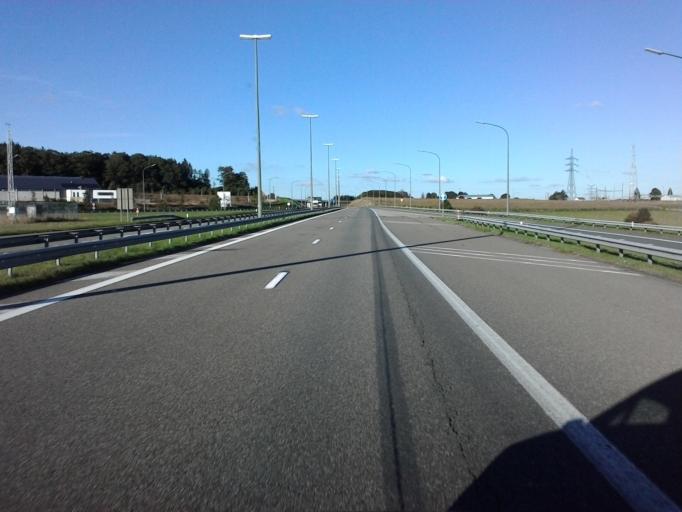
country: BE
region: Wallonia
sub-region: Province du Luxembourg
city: Houffalize
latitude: 50.1468
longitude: 5.7870
